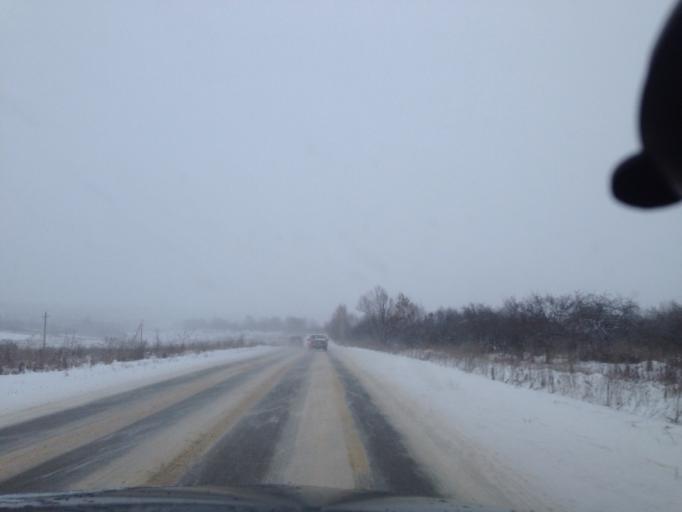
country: RU
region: Tula
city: Bolokhovo
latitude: 54.0687
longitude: 37.8052
